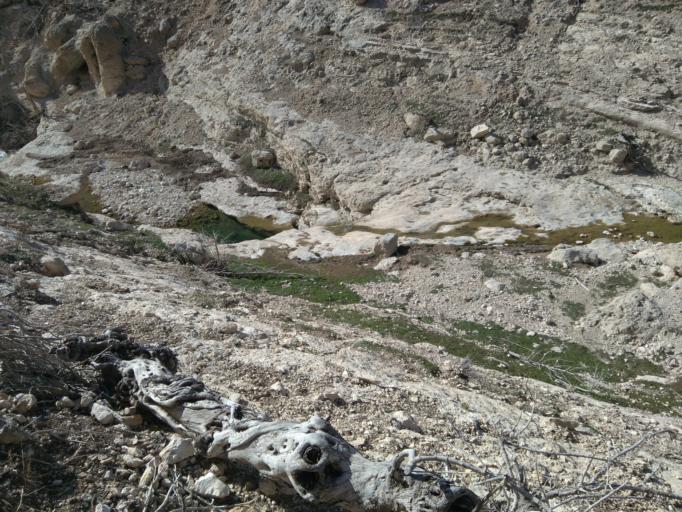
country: ES
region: Valencia
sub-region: Provincia de Valencia
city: Sumacarcer
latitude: 39.1599
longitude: -0.6603
